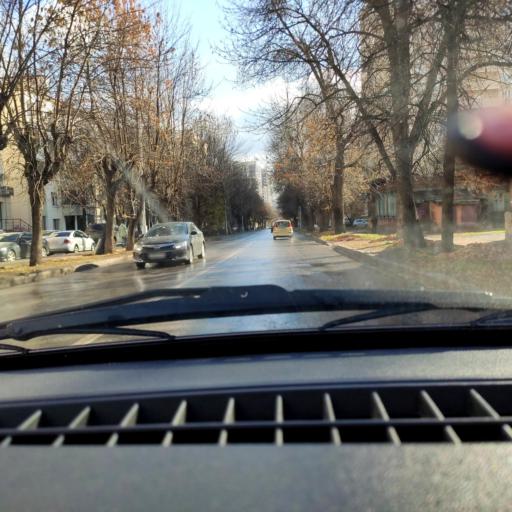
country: RU
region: Bashkortostan
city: Ufa
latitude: 54.7237
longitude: 55.9575
